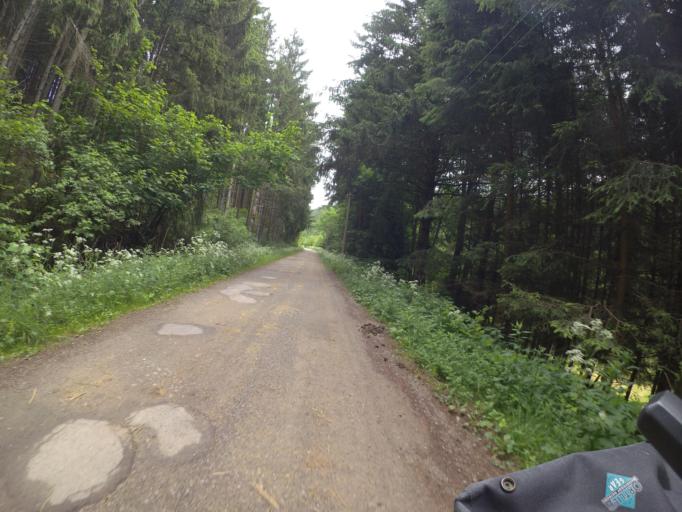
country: DE
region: North Rhine-Westphalia
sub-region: Regierungsbezirk Koln
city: Hellenthal
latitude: 50.4429
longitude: 6.4116
